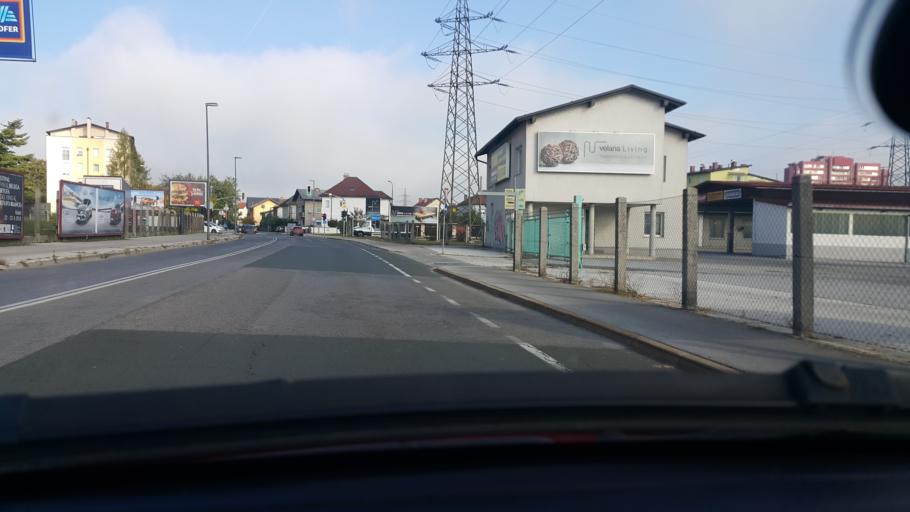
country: SI
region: Ljubljana
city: Ljubljana
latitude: 46.0633
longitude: 14.5376
